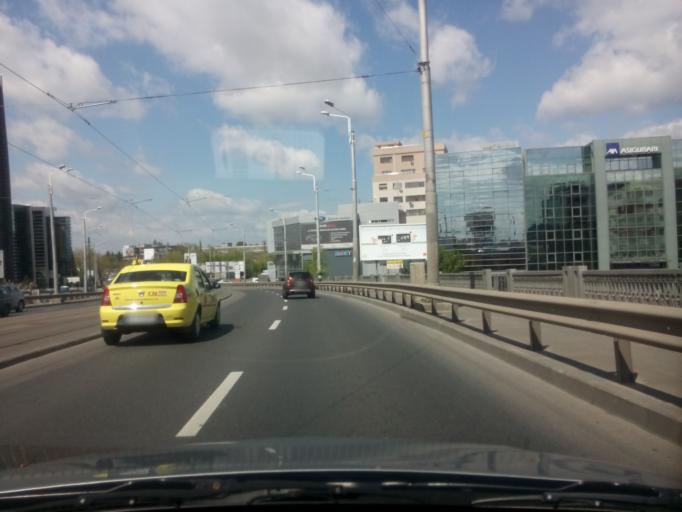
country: RO
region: Bucuresti
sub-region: Municipiul Bucuresti
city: Bucharest
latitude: 44.4898
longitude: 26.0913
